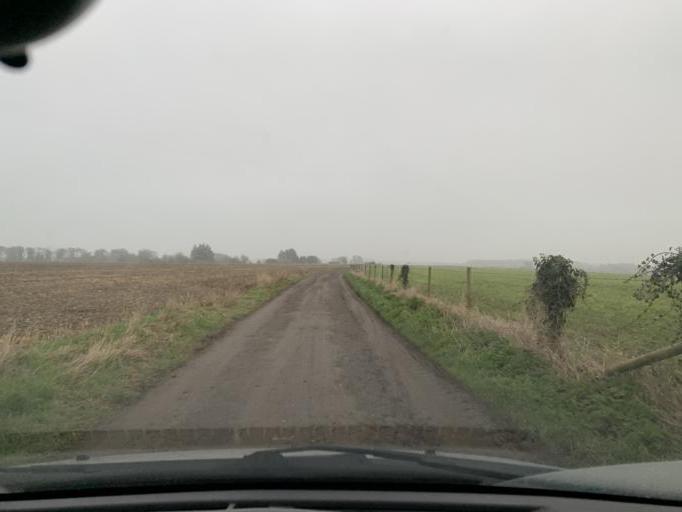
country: GB
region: England
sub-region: Wiltshire
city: Shrewton
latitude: 51.1955
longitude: -1.8950
